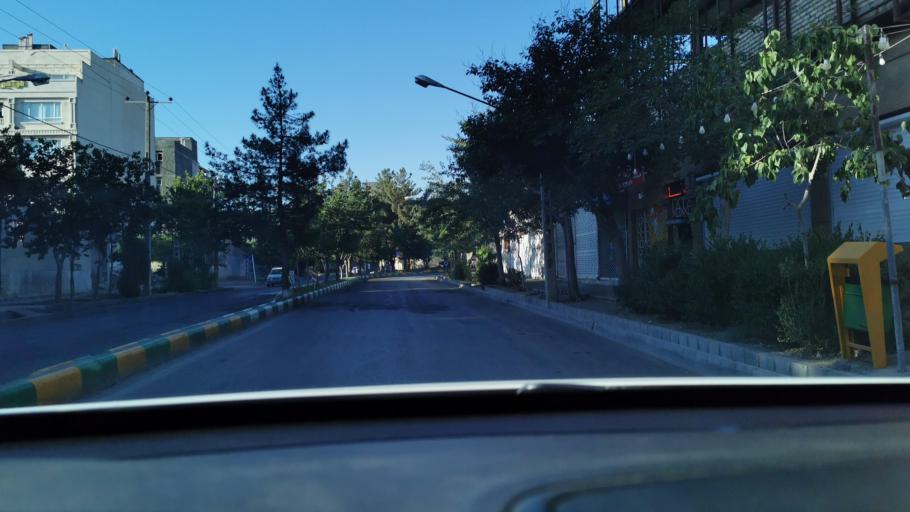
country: IR
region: Razavi Khorasan
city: Mashhad
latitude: 36.3610
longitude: 59.4904
